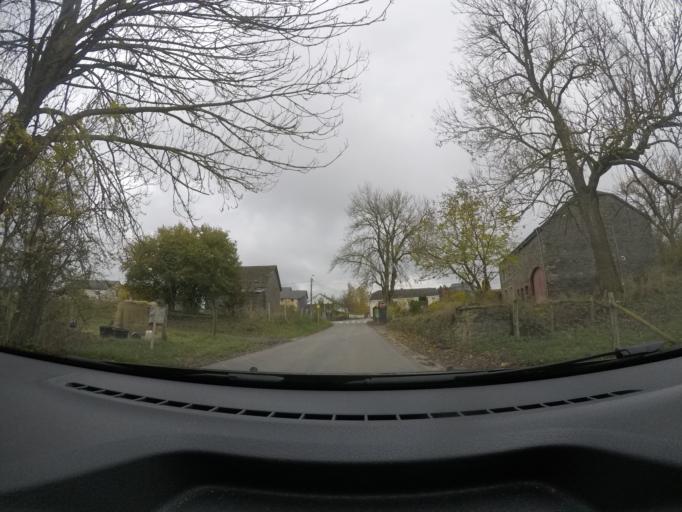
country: BE
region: Wallonia
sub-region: Province du Luxembourg
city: Bertogne
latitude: 50.0857
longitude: 5.7056
